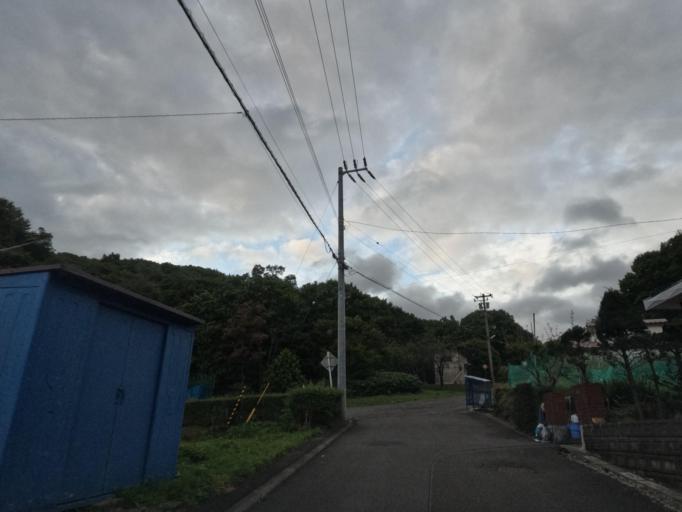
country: JP
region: Hokkaido
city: Muroran
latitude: 42.3669
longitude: 140.9653
